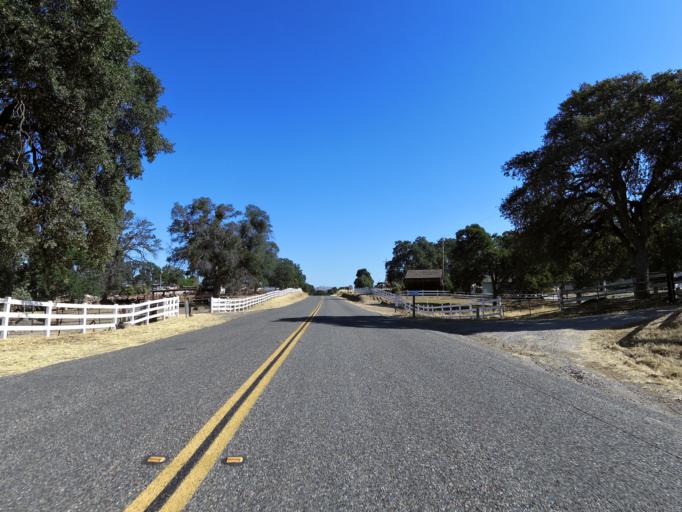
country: US
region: California
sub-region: Mariposa County
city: Mariposa
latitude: 37.4492
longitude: -120.1034
